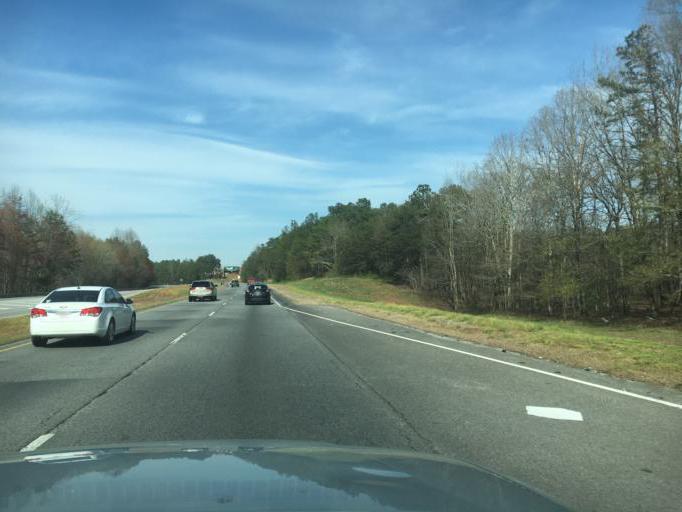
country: US
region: Georgia
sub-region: Hall County
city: Lula
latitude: 34.4145
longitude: -83.6591
